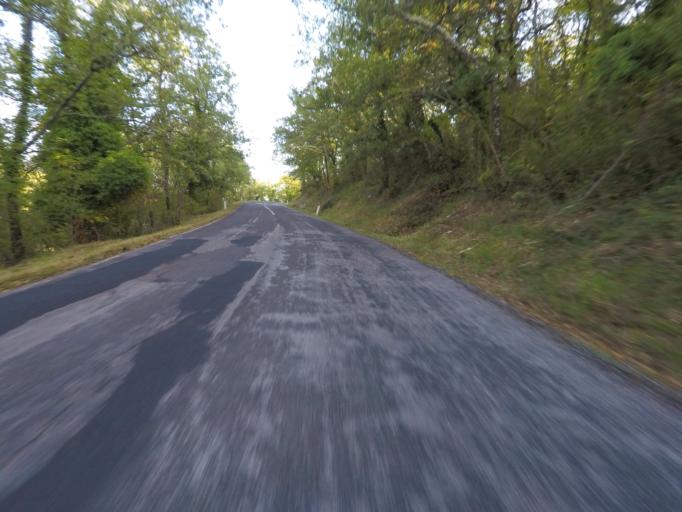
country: IT
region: Tuscany
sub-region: Provincia di Siena
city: Radda in Chianti
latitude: 43.4601
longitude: 11.3862
